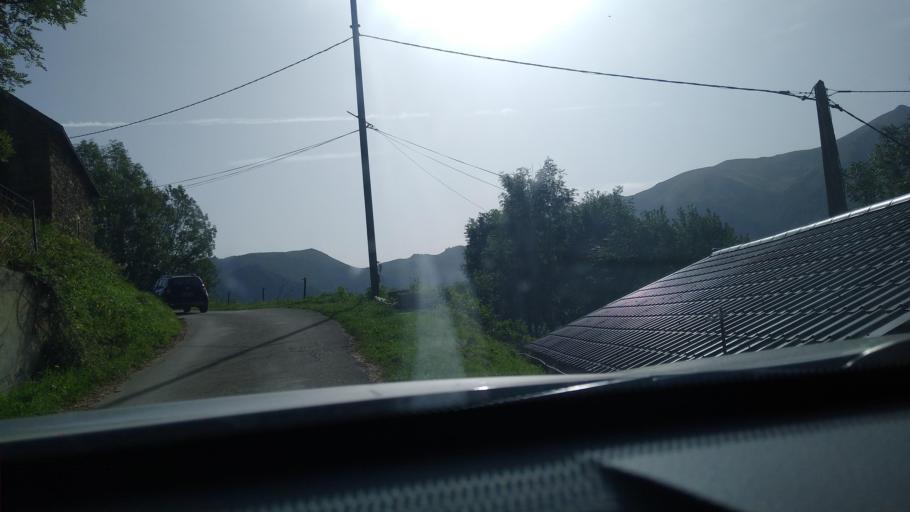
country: FR
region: Midi-Pyrenees
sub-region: Departement de l'Ariege
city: Saint-Girons
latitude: 42.7926
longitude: 1.1709
